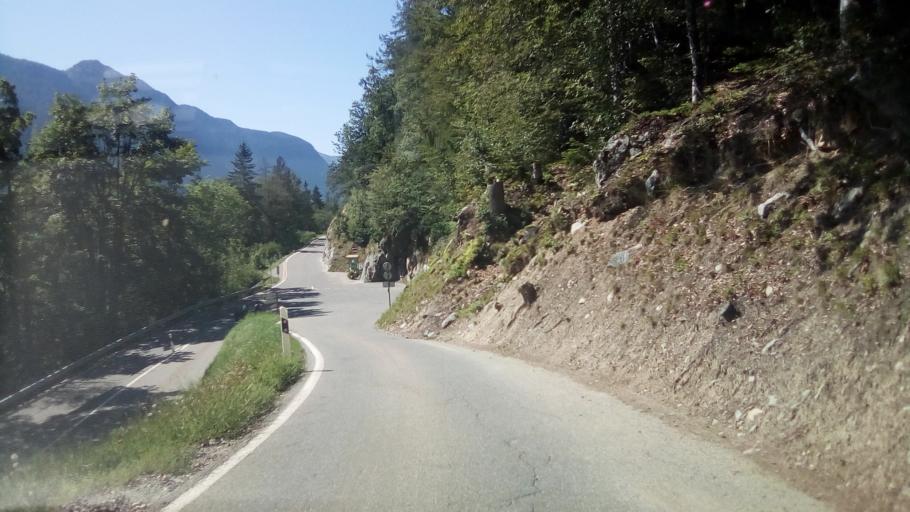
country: CH
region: Valais
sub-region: Saint-Maurice District
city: Salvan
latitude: 46.1231
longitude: 7.0180
